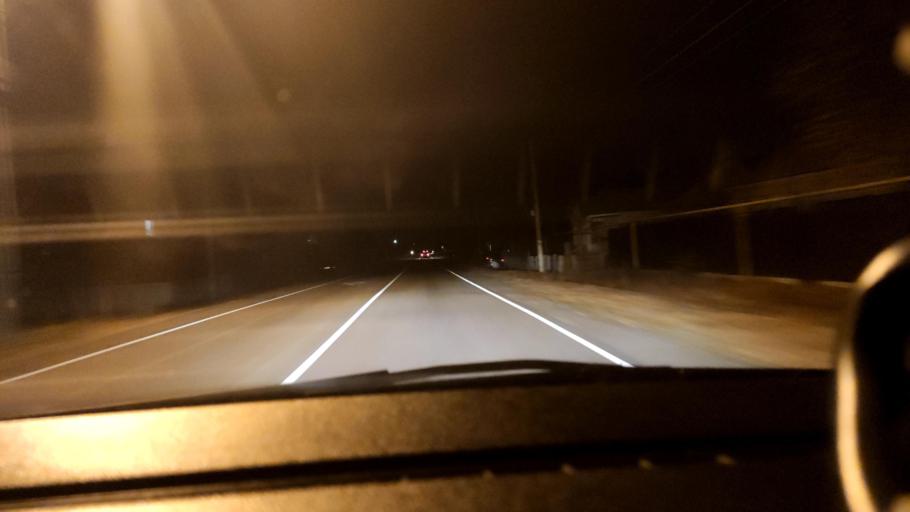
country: RU
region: Voronezj
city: Shilovo
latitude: 51.5813
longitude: 39.0366
